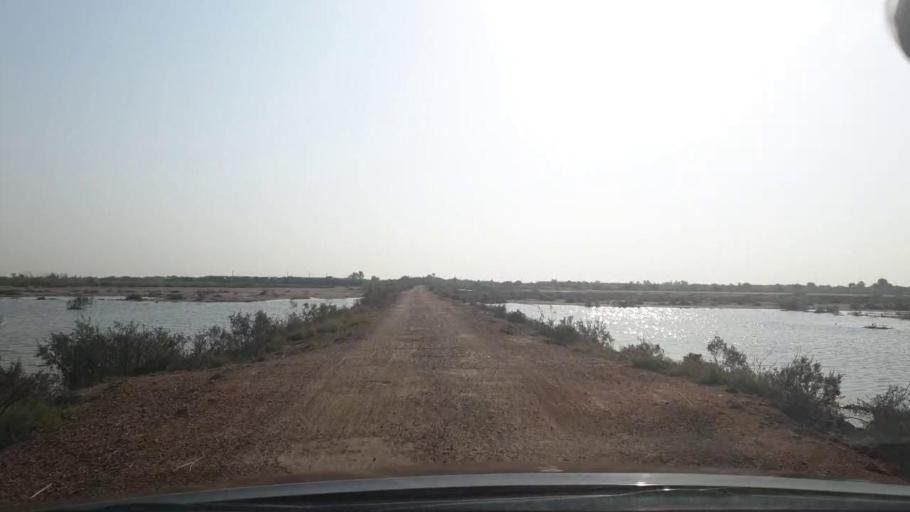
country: PK
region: Sindh
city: Tando Bago
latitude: 24.6510
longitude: 69.1333
